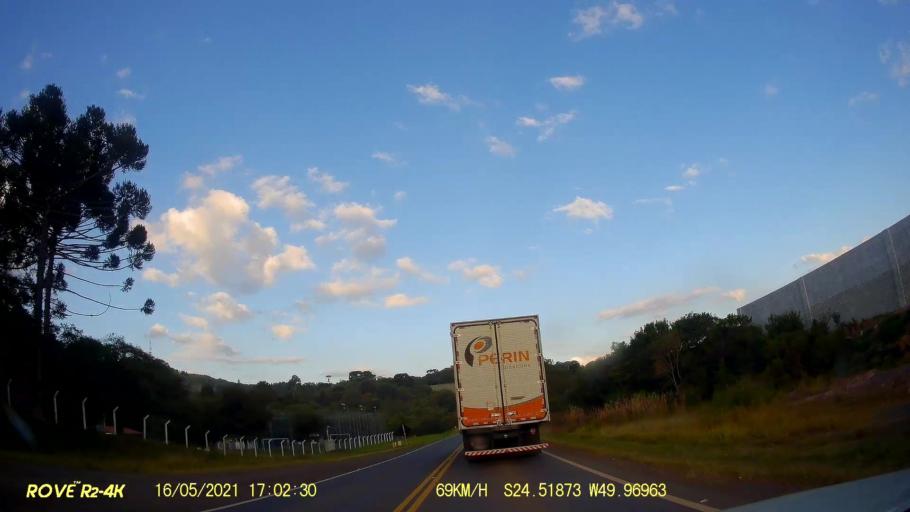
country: BR
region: Parana
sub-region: Pirai Do Sul
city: Pirai do Sul
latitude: -24.5188
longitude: -49.9696
